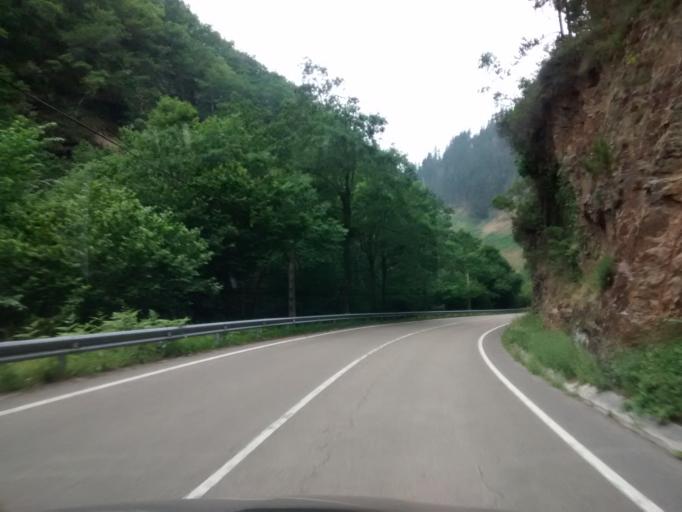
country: ES
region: Cantabria
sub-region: Provincia de Cantabria
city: Ruente
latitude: 43.1600
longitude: -4.2433
